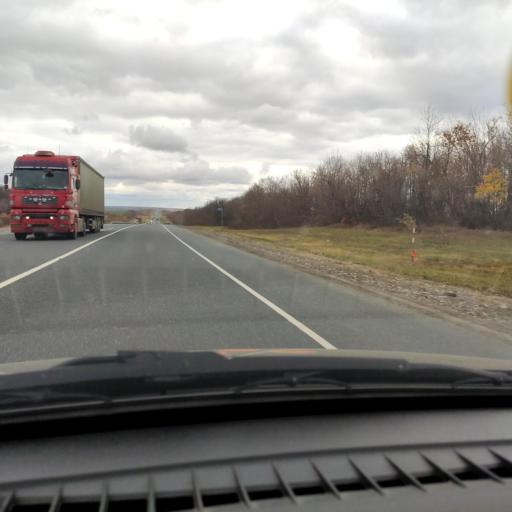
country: RU
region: Samara
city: Mezhdurechensk
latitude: 53.2594
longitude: 49.0857
